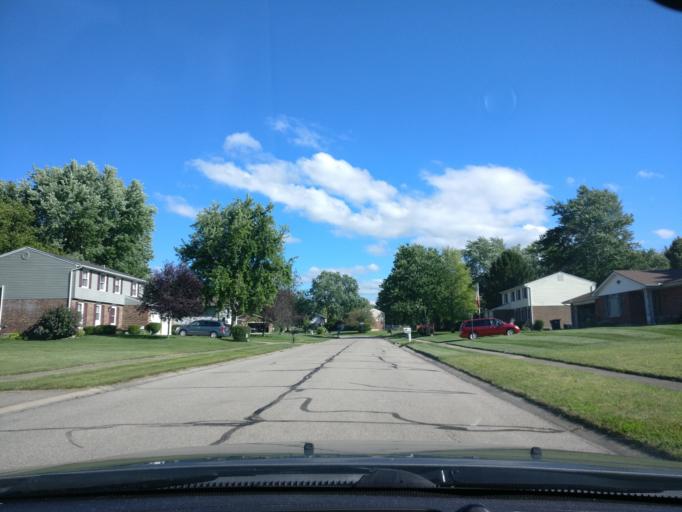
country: US
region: Ohio
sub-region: Montgomery County
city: Centerville
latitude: 39.6022
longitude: -84.1759
